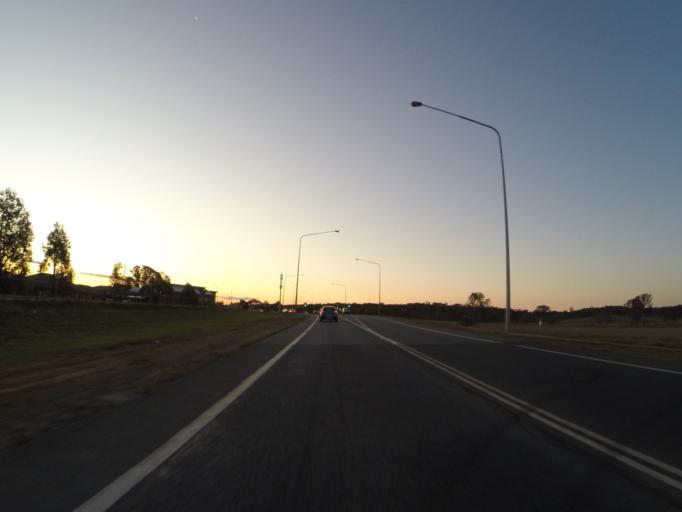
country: AU
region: Australian Capital Territory
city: Kaleen
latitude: -35.1858
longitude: 149.1573
